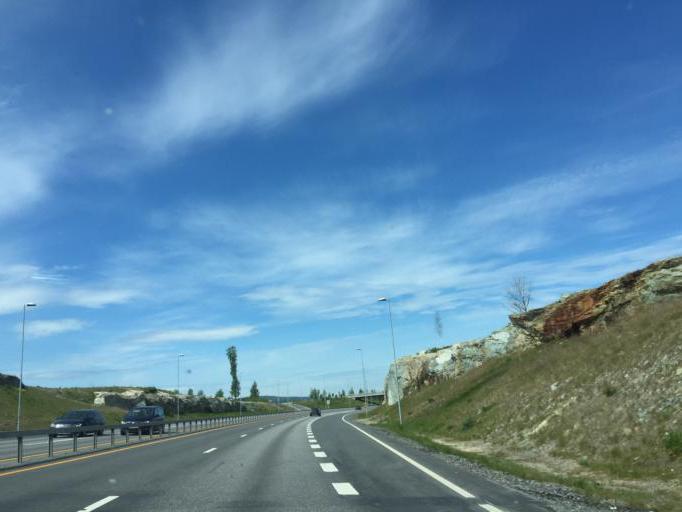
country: NO
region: Hedmark
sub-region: Kongsvinger
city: Spetalen
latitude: 60.2073
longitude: 11.8963
